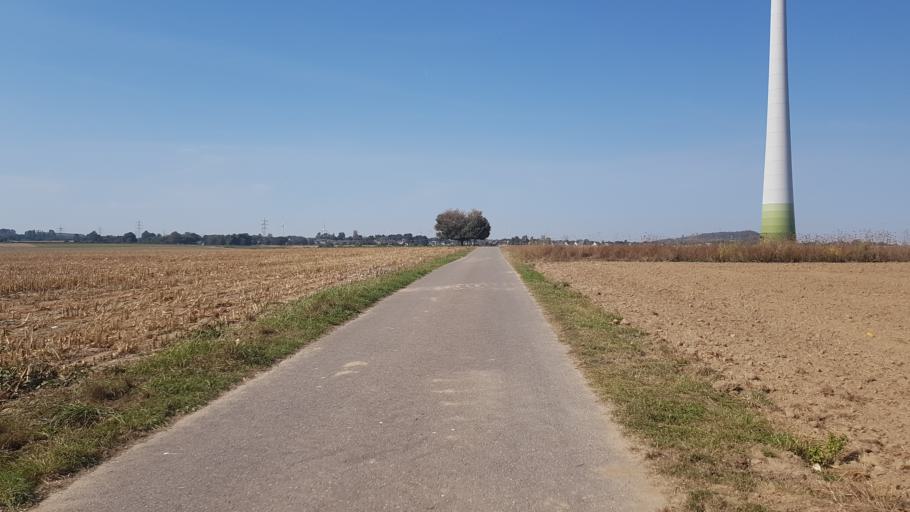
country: DE
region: North Rhine-Westphalia
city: Siersdorf
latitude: 50.8958
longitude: 6.2086
